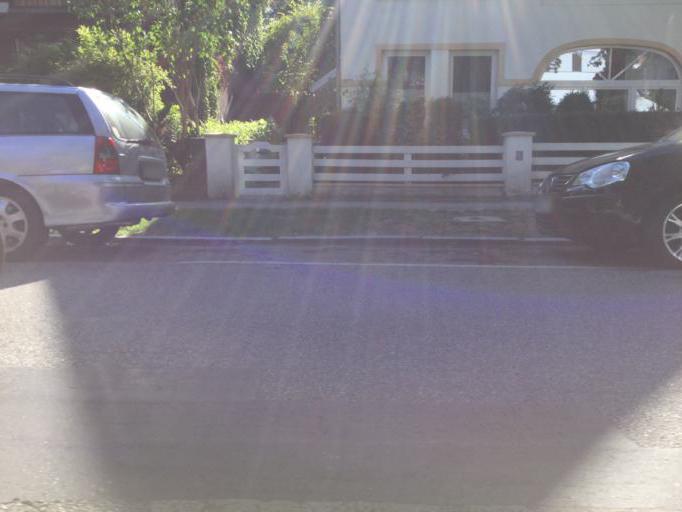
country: DE
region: Hamburg
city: Fuhlsbuettel
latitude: 53.6346
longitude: 10.0254
